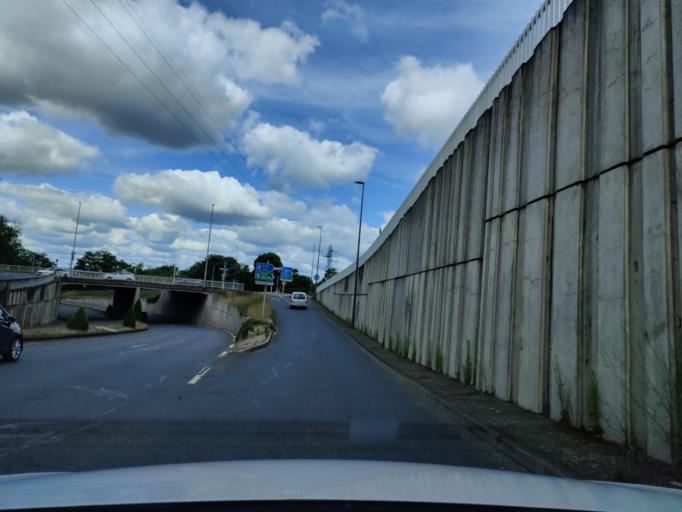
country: FR
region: Auvergne
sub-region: Departement de l'Allier
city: Desertines
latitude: 46.3459
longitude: 2.6102
